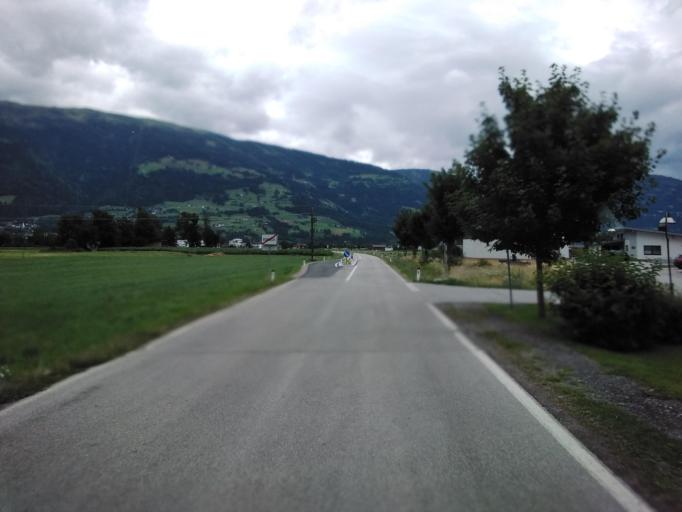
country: AT
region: Tyrol
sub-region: Politischer Bezirk Lienz
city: Amlach
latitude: 46.8152
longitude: 12.7628
